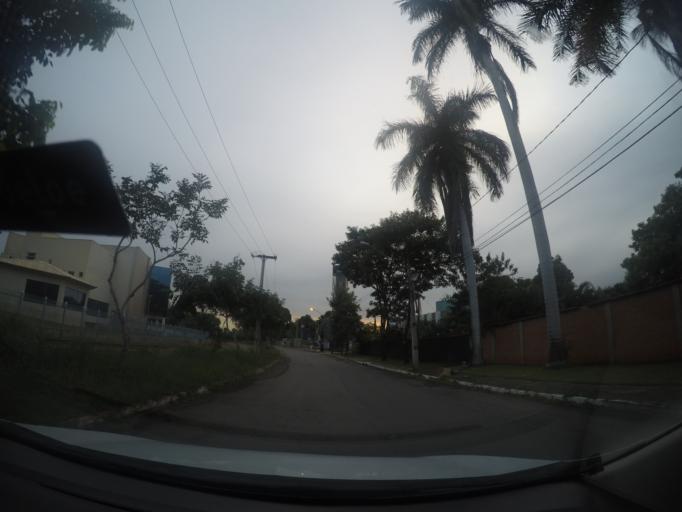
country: BR
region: Goias
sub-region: Goiania
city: Goiania
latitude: -16.6398
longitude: -49.2464
